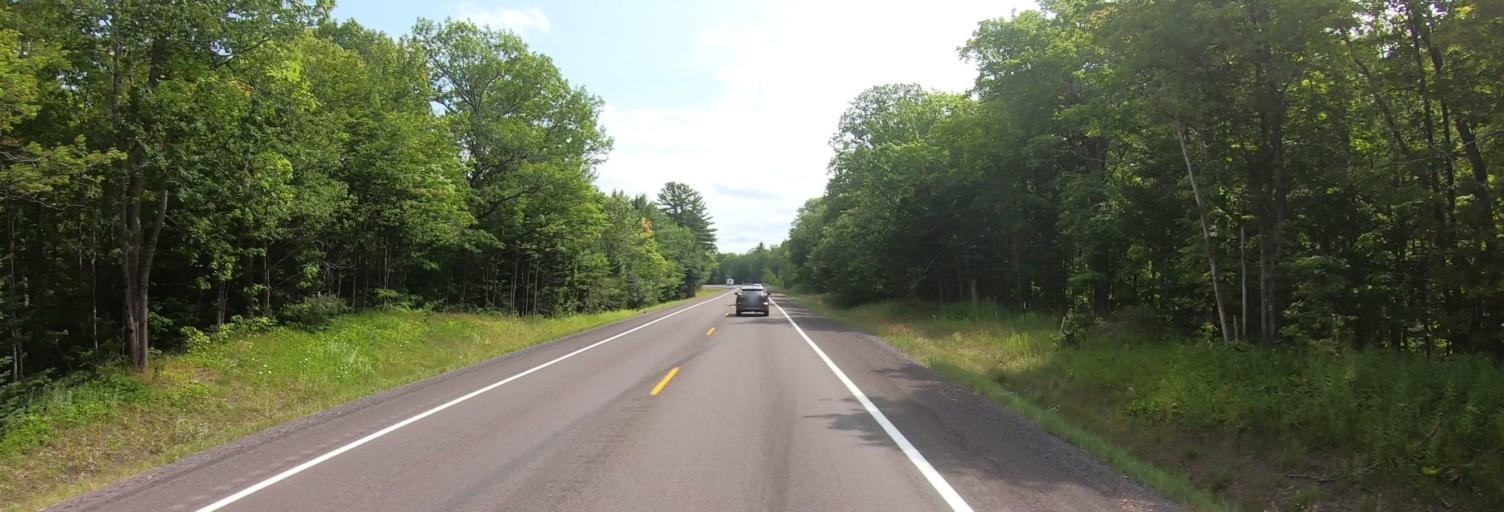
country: US
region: Michigan
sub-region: Houghton County
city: Hancock
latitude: 46.9746
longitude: -88.7804
